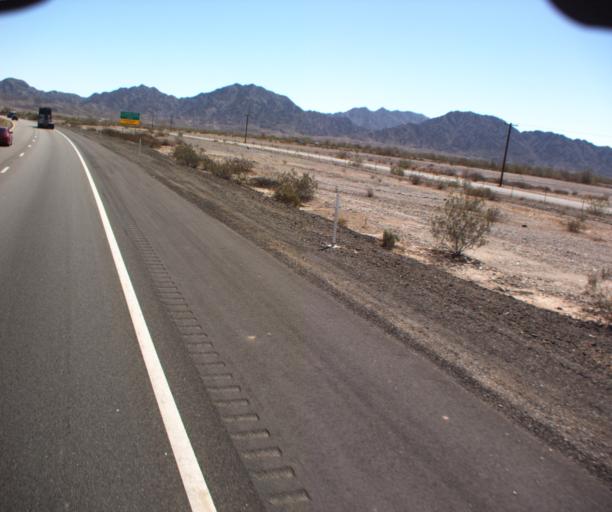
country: US
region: Arizona
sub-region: Yuma County
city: Fortuna Foothills
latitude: 32.6615
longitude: -114.3790
